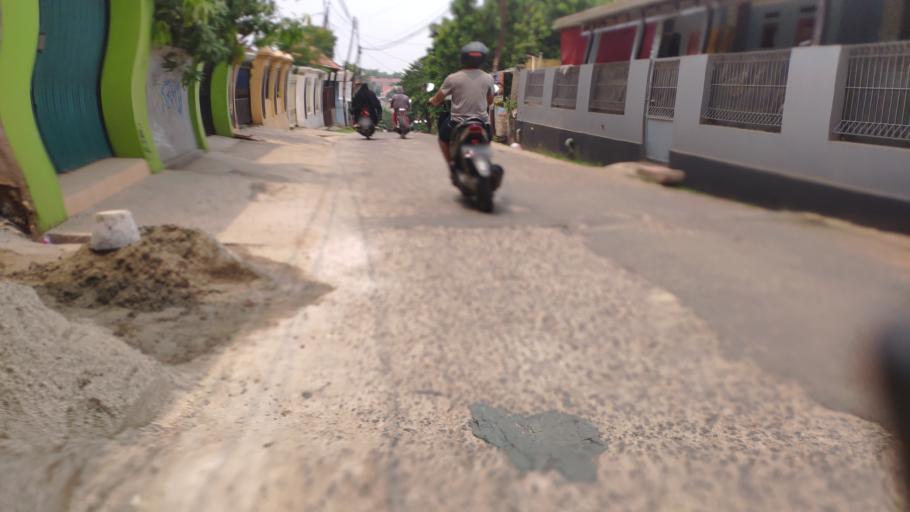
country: ID
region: West Java
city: Sawangan
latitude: -6.3839
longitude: 106.7881
